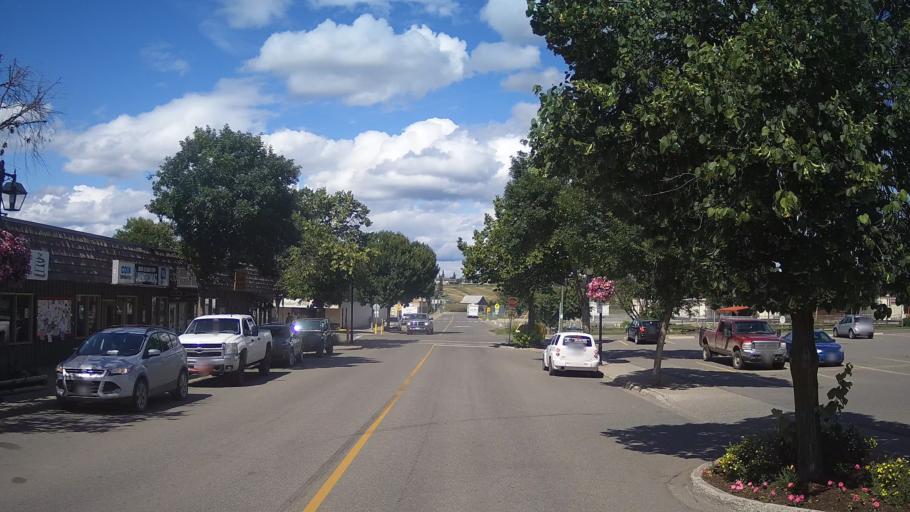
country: CA
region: British Columbia
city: Cache Creek
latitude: 51.6458
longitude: -121.2950
